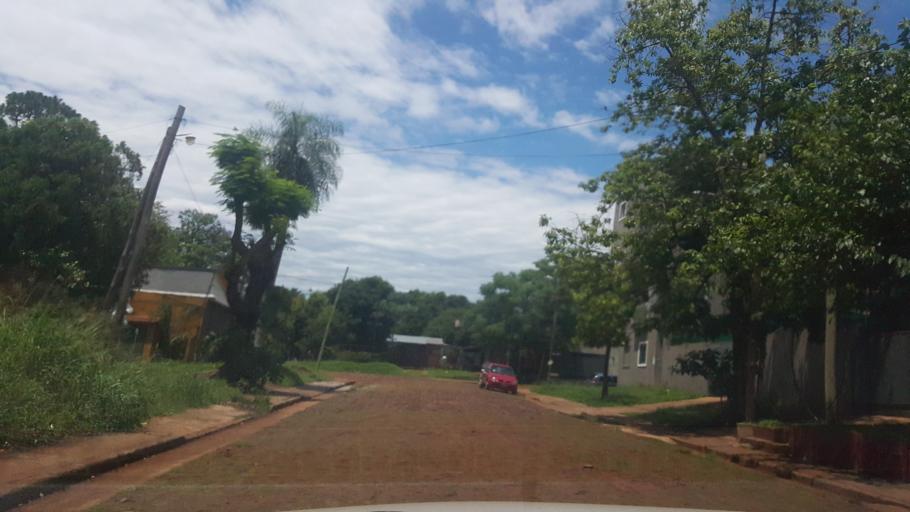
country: AR
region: Misiones
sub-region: Departamento de Capital
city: Posadas
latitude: -27.3904
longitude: -55.9147
